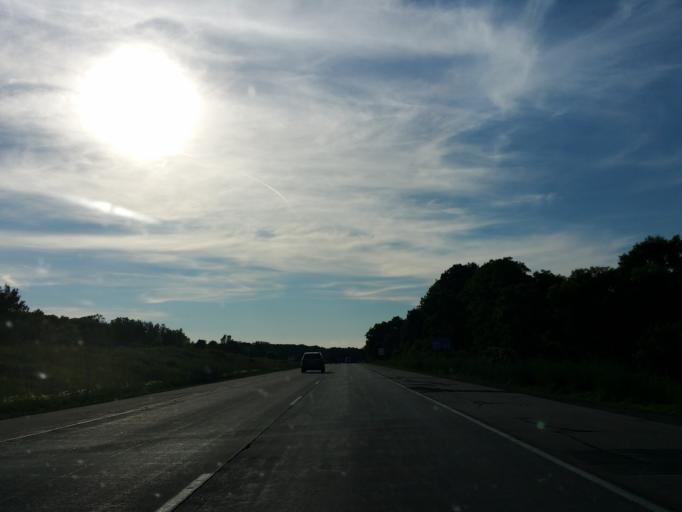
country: US
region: Wisconsin
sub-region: Columbia County
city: Portage
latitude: 43.5004
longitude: -89.5060
